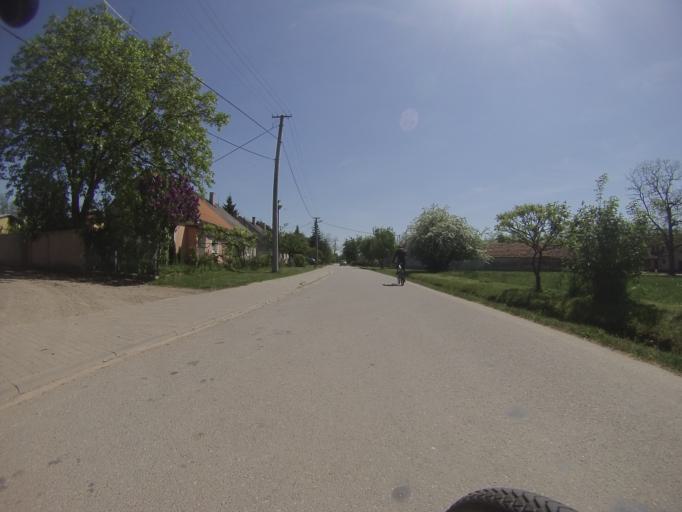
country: CZ
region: South Moravian
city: Novosedly
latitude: 48.8054
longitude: 16.4944
